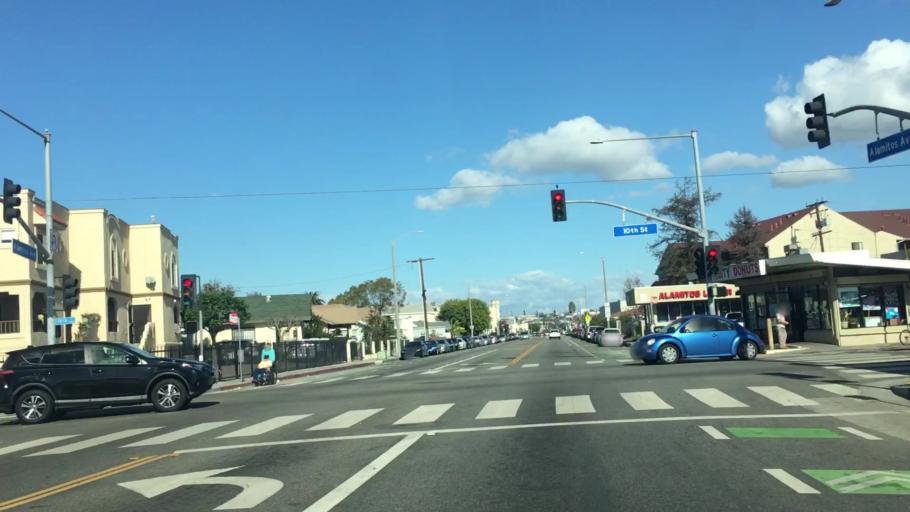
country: US
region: California
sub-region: Los Angeles County
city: Long Beach
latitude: 33.7788
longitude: -118.1791
